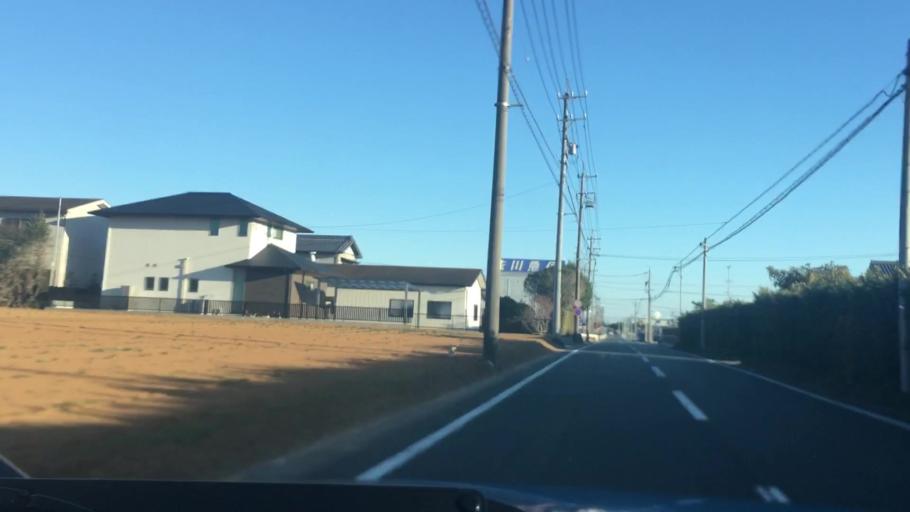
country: JP
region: Shizuoka
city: Hamamatsu
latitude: 34.7641
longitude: 137.6863
